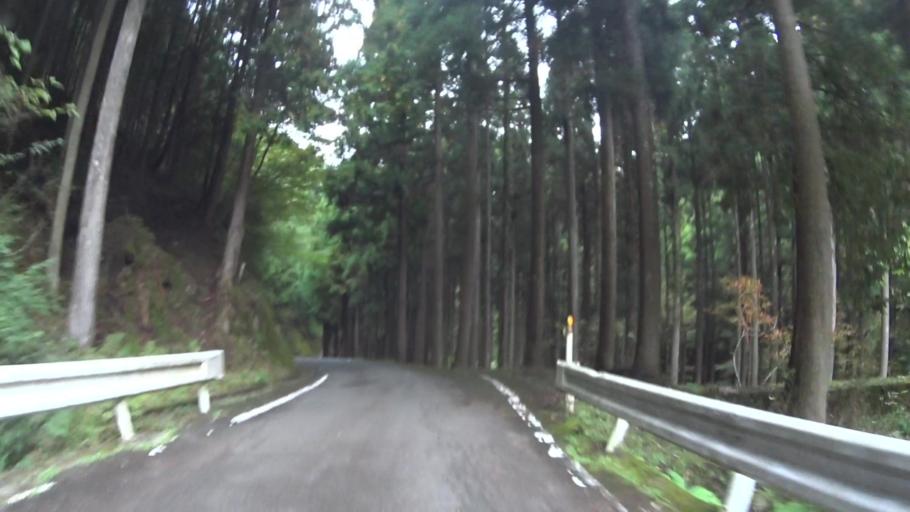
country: JP
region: Fukui
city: Obama
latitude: 35.2775
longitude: 135.6985
